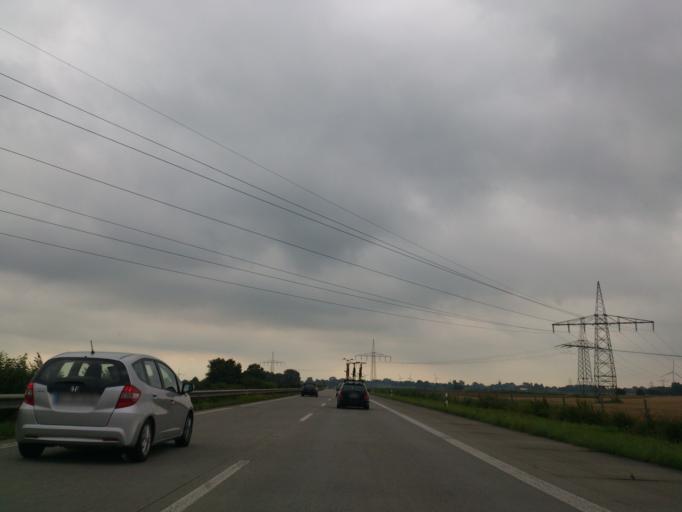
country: DE
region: Schleswig-Holstein
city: Rethwisch
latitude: 53.8580
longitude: 9.5754
